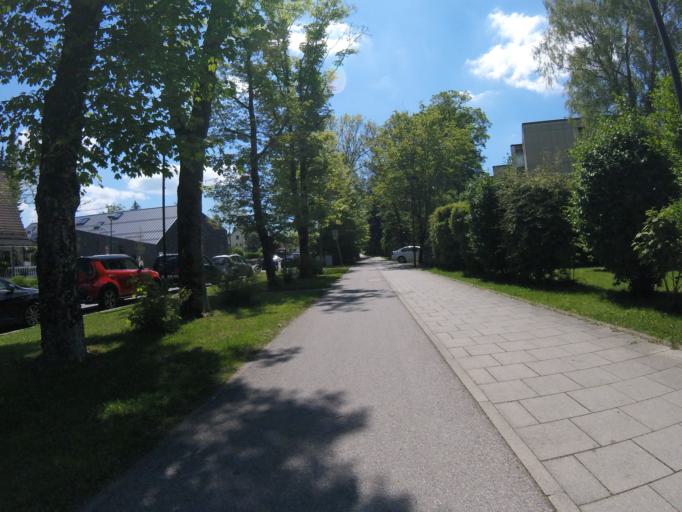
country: DE
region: Bavaria
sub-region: Upper Bavaria
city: Neubiberg
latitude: 48.0707
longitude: 11.6563
